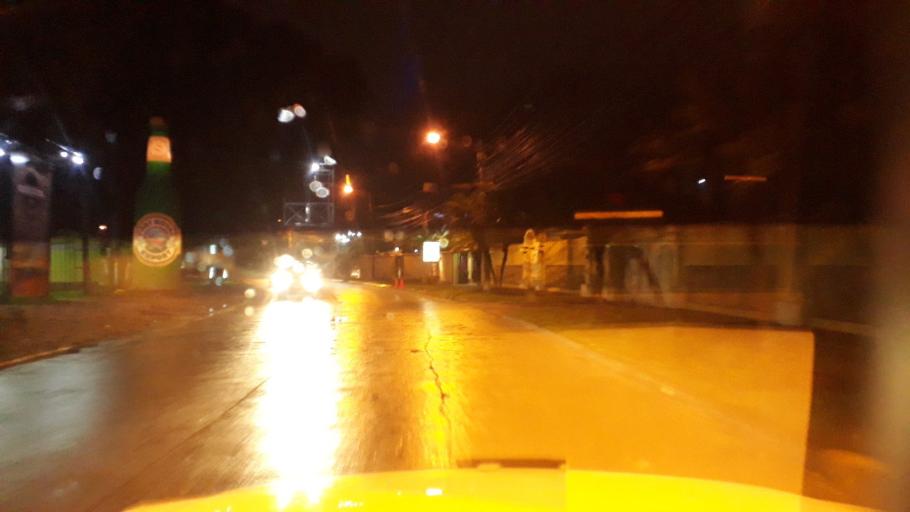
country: HN
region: Cortes
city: El Zapotal del Norte
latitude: 15.5248
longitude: -88.0344
